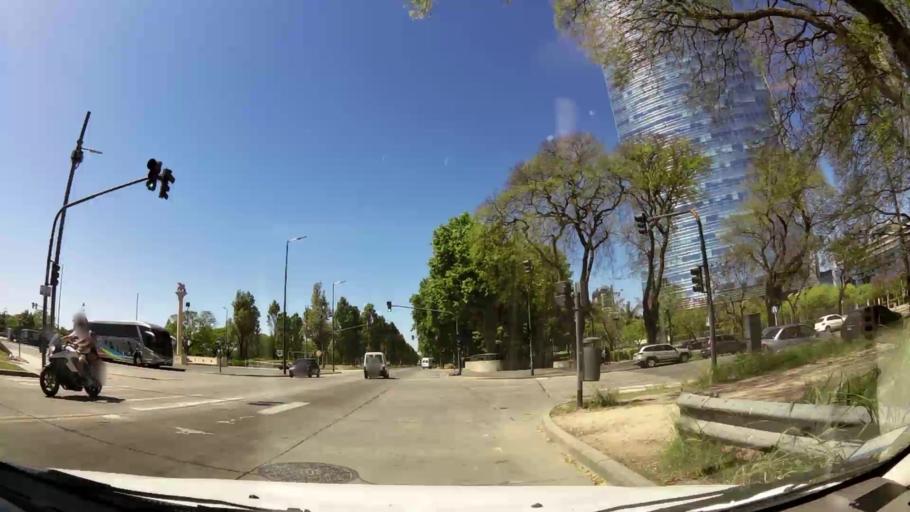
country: AR
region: Buenos Aires F.D.
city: Buenos Aires
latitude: -34.6046
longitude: -58.3617
